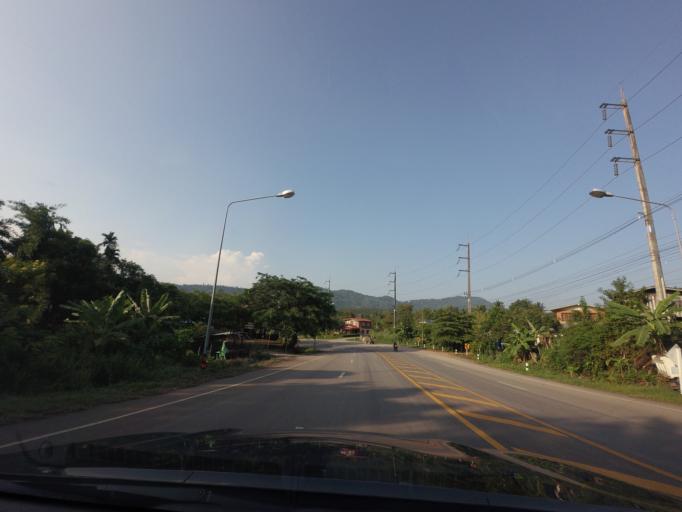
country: TH
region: Loei
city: Dan Sai
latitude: 17.2073
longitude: 101.1593
